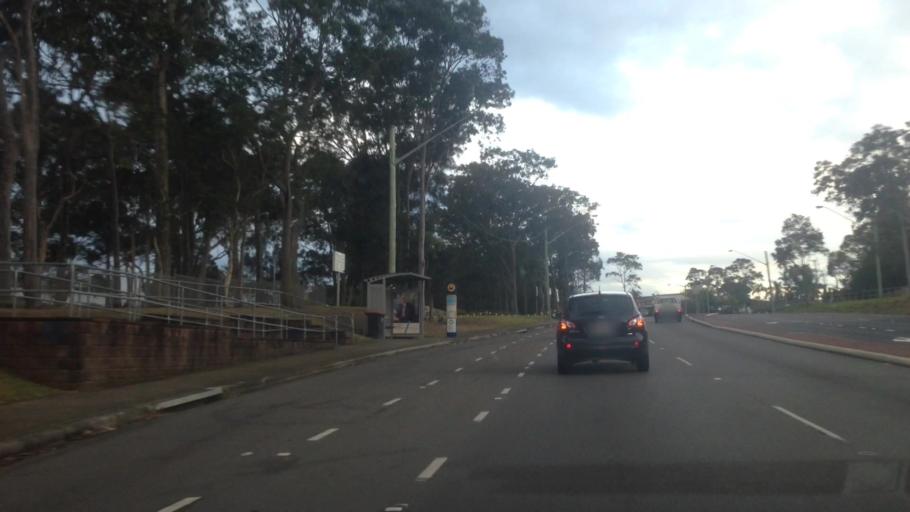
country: AU
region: New South Wales
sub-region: Wyong Shire
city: Kanwal
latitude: -33.2622
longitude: 151.4819
